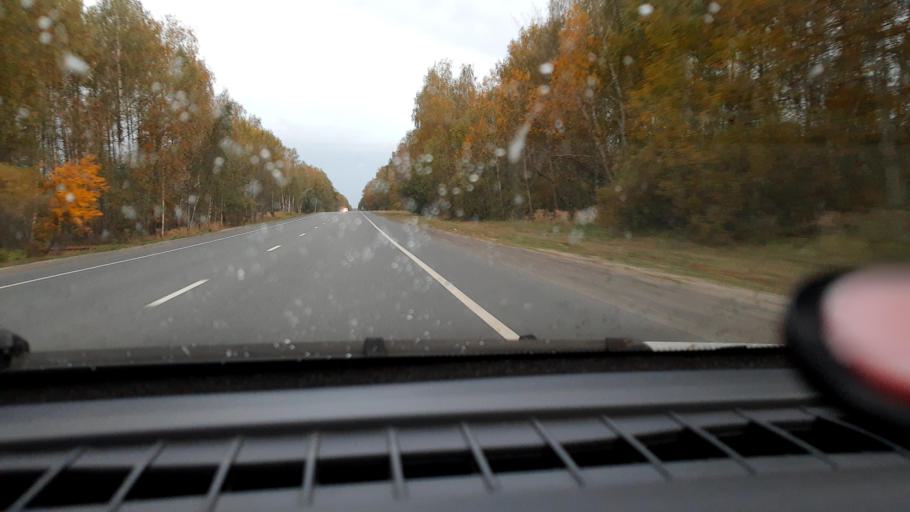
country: RU
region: Vladimir
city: Orgtrud
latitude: 56.2048
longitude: 40.7299
